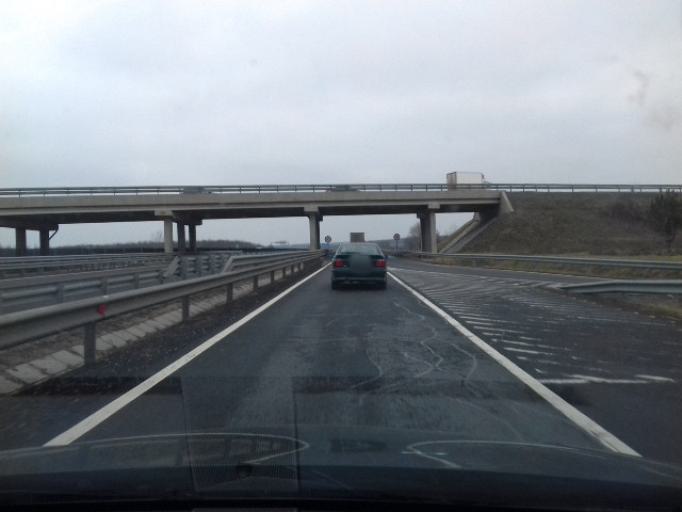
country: HU
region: Szabolcs-Szatmar-Bereg
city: Nagykallo
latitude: 47.8926
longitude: 21.8018
